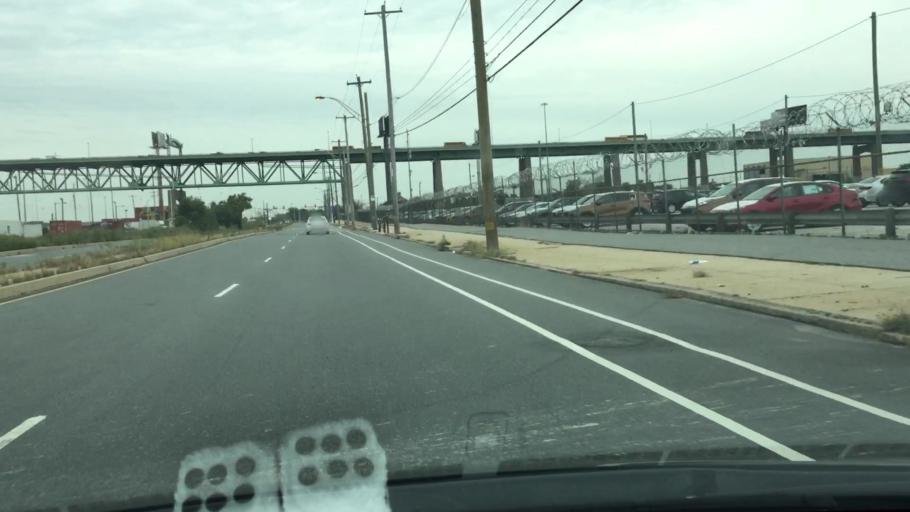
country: US
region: New Jersey
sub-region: Camden County
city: Camden
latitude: 39.9109
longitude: -75.1387
